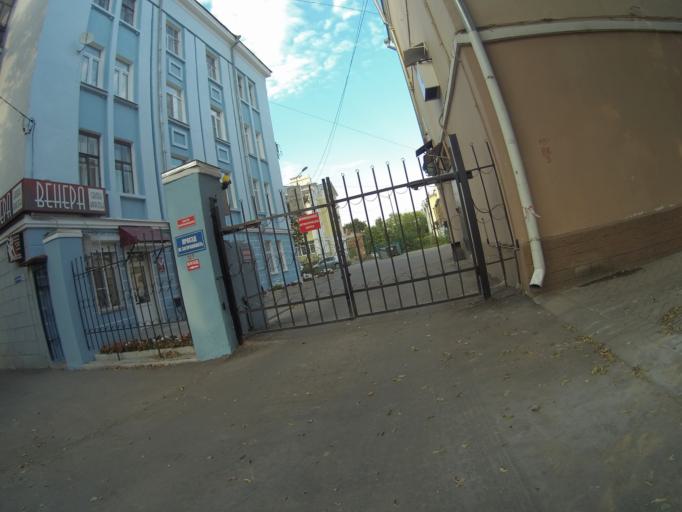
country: RU
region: Vladimir
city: Vladimir
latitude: 56.1331
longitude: 40.4168
